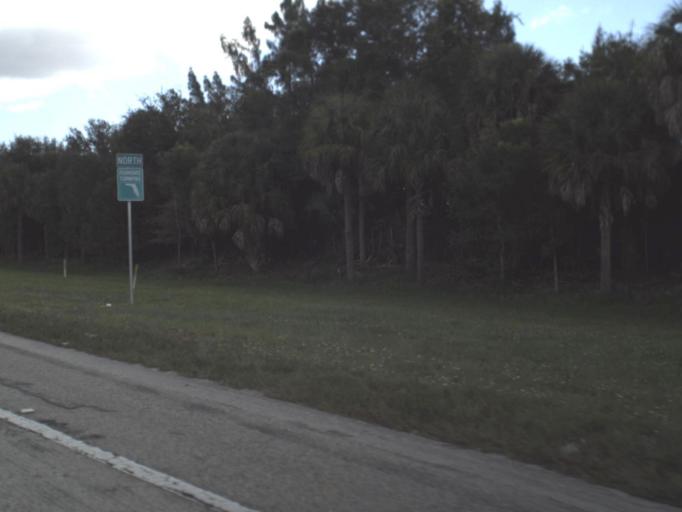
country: US
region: Florida
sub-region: Palm Beach County
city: Plantation Mobile Home Park
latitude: 26.7160
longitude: -80.1365
